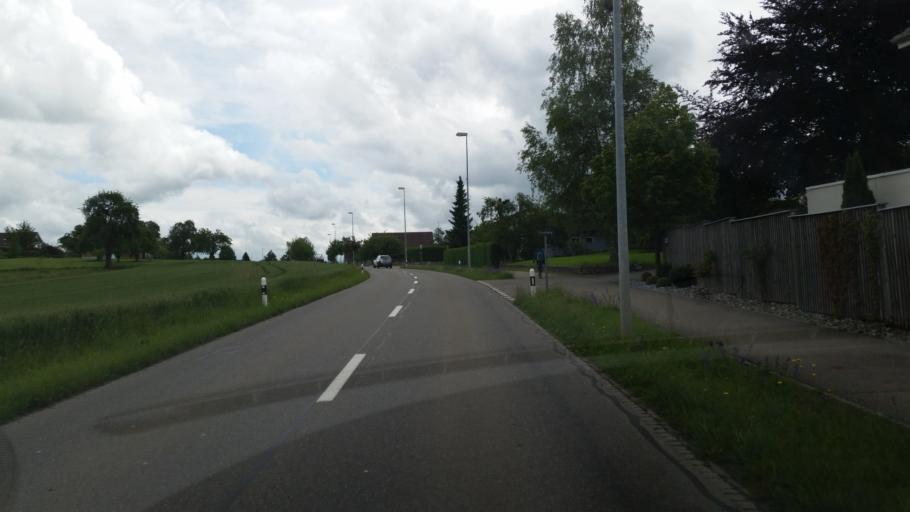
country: CH
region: Aargau
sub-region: Bezirk Bremgarten
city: Berikon
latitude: 47.3389
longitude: 8.3833
